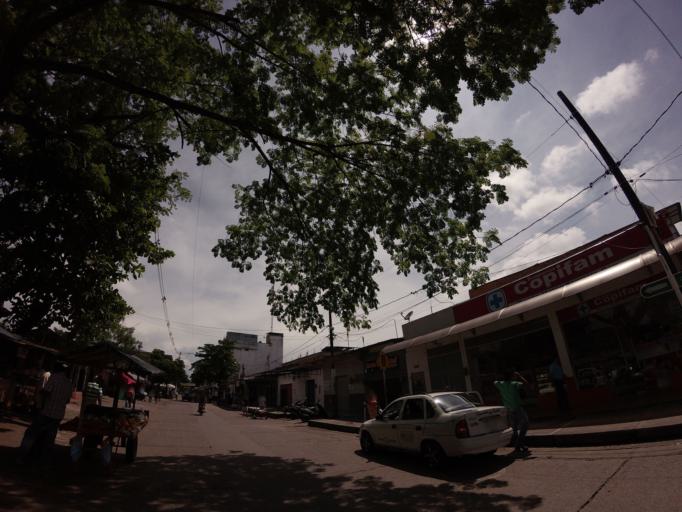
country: CO
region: Caldas
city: La Dorada
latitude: 5.4520
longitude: -74.6638
